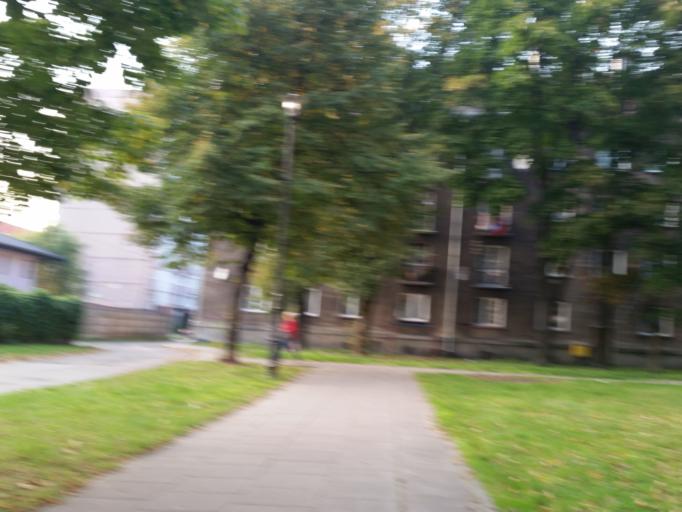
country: PL
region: Silesian Voivodeship
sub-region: Sosnowiec
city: Sosnowiec
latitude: 50.2694
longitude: 19.1219
